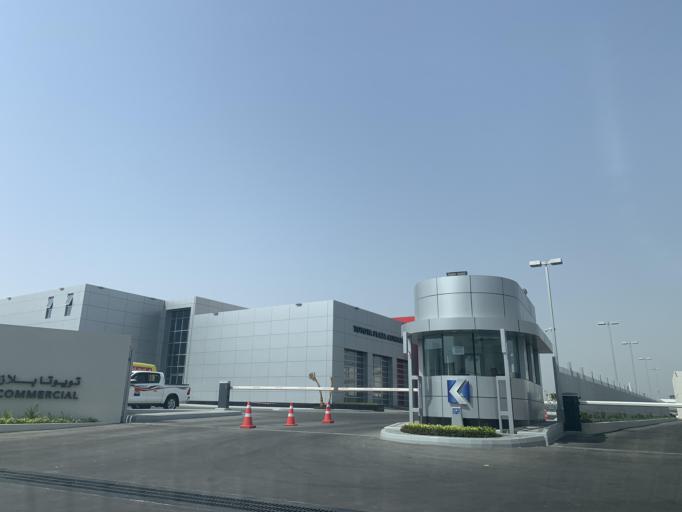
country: BH
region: Northern
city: Madinat `Isa
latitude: 26.1873
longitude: 50.5427
